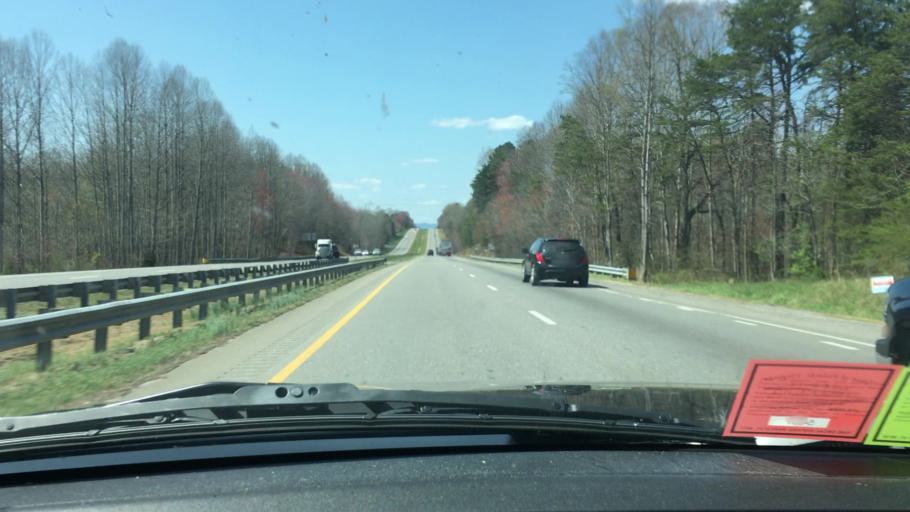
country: US
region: North Carolina
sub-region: Surry County
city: Pilot Mountain
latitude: 36.4113
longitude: -80.5028
